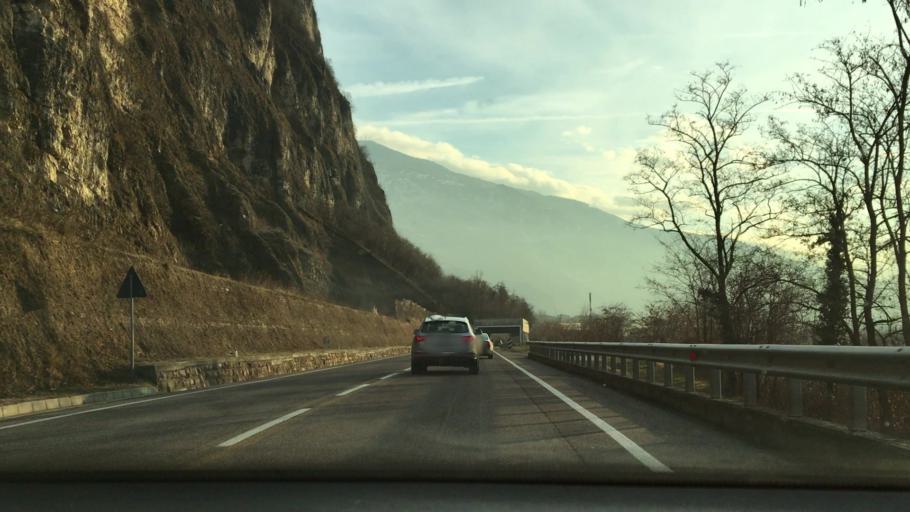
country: IT
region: Trentino-Alto Adige
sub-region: Provincia di Trento
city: Besenello
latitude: 45.9595
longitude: 11.1102
